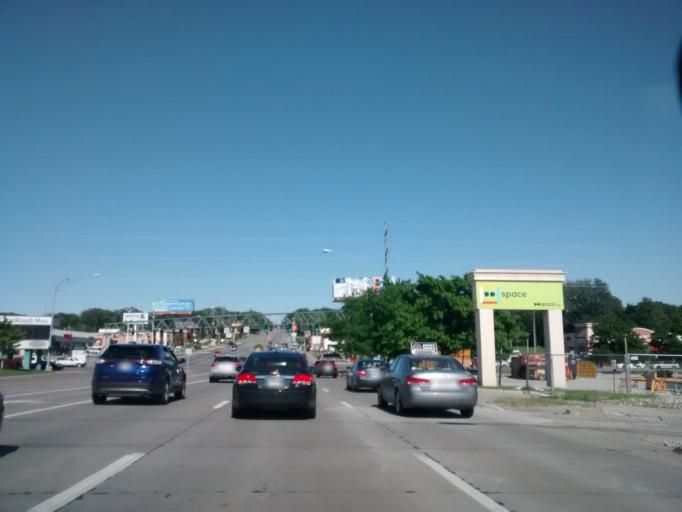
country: US
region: Nebraska
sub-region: Douglas County
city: Ralston
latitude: 41.2596
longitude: -96.0253
